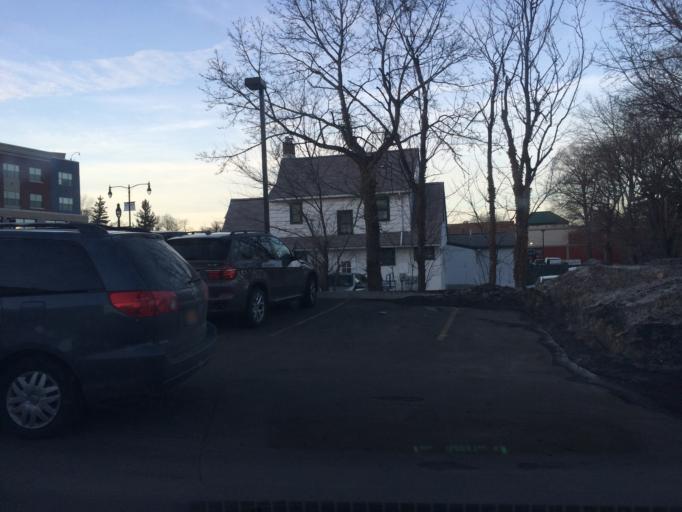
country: US
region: New York
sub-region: Monroe County
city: Rochester
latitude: 43.1235
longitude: -77.6176
